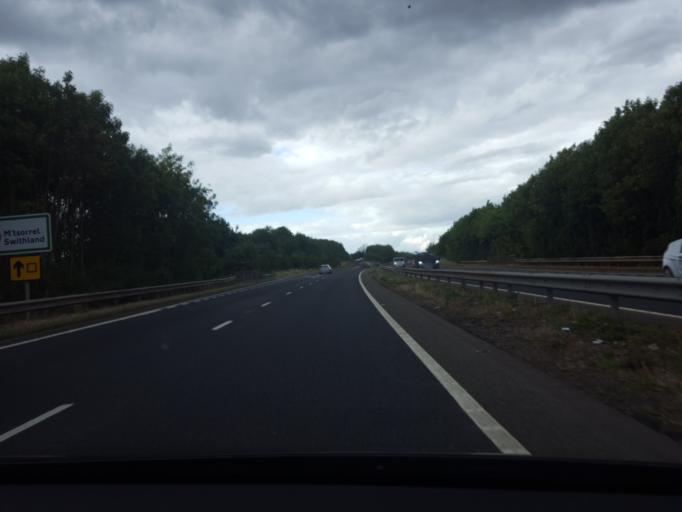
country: GB
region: England
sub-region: Leicestershire
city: Mountsorrel
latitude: 52.7147
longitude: -1.1257
